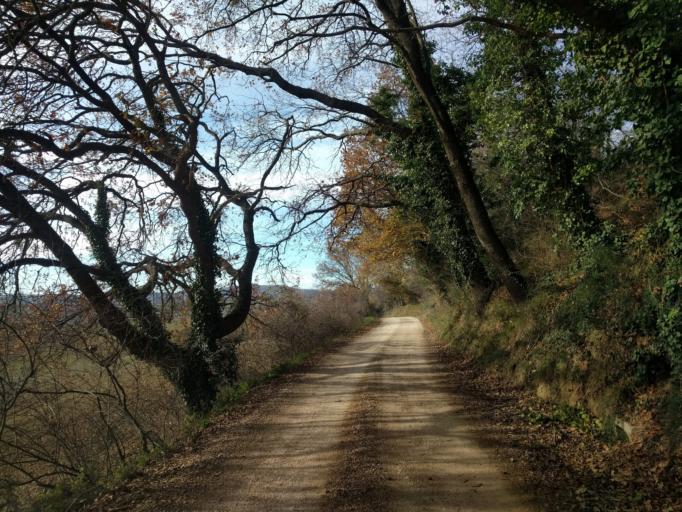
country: IT
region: The Marches
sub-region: Provincia di Pesaro e Urbino
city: Cuccurano
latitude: 43.8082
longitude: 12.9477
